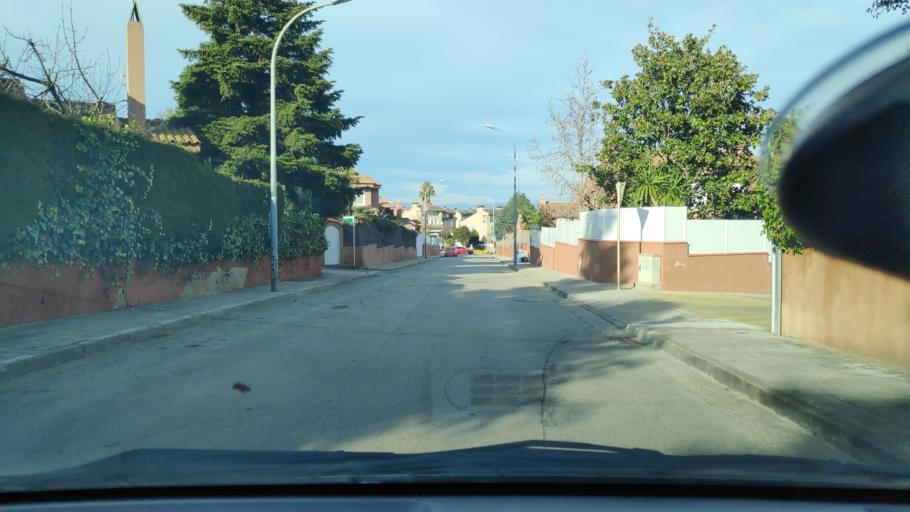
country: ES
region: Catalonia
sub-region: Provincia de Barcelona
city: Sant Quirze del Valles
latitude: 41.5271
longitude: 2.0699
